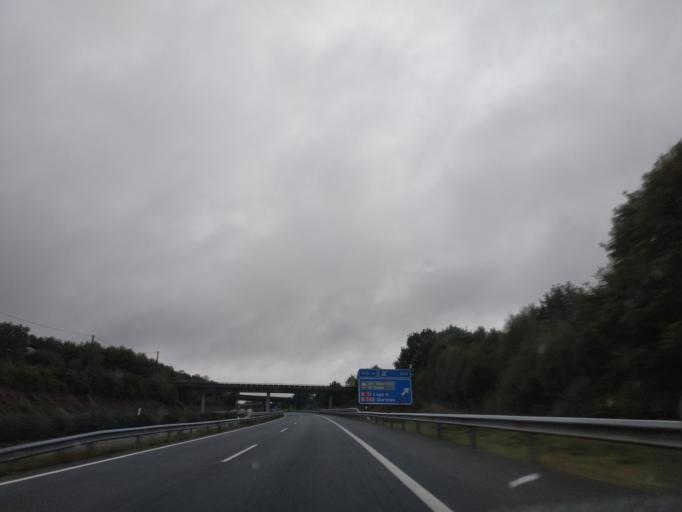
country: ES
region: Galicia
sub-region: Provincia de Lugo
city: Lugo
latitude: 43.0650
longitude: -7.5704
